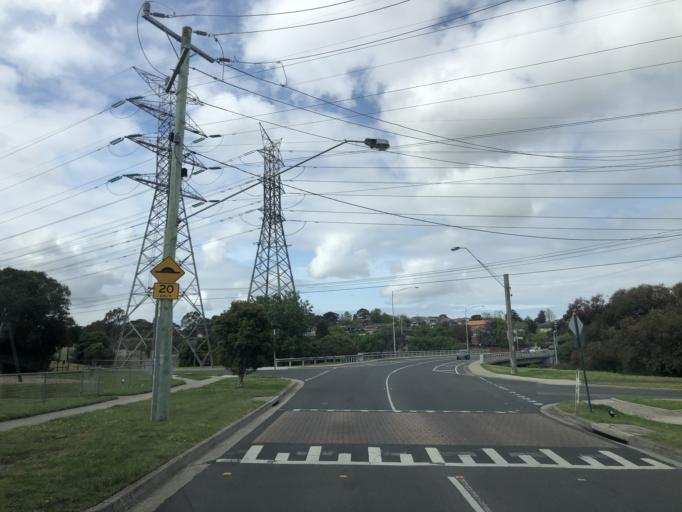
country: AU
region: Victoria
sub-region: Monash
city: Chadstone
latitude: -37.8837
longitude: 145.0966
